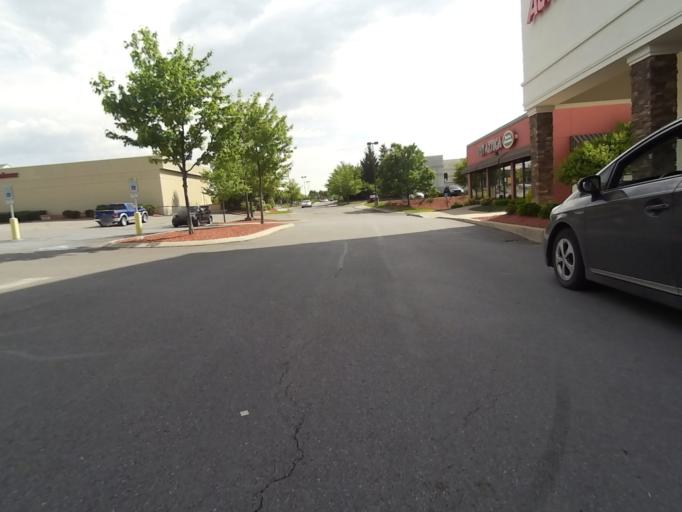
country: US
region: Pennsylvania
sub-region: Centre County
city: Houserville
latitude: 40.8340
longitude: -77.8040
